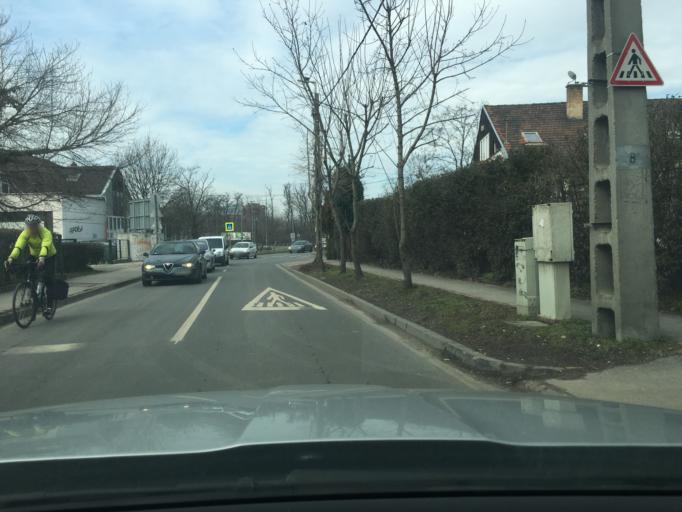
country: HU
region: Budapest
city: Budapest XIX. keruelet
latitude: 47.4608
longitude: 19.1540
